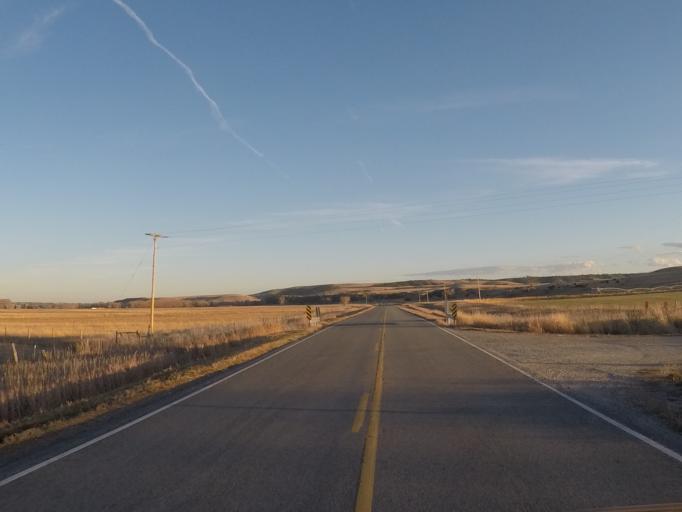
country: US
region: Montana
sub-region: Sweet Grass County
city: Big Timber
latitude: 45.7964
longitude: -109.8587
